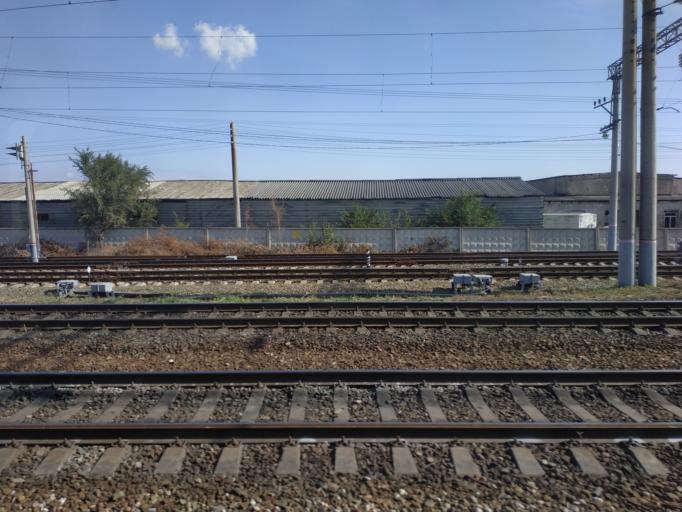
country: RU
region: Volgograd
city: Gumrak
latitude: 48.7869
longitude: 44.3709
